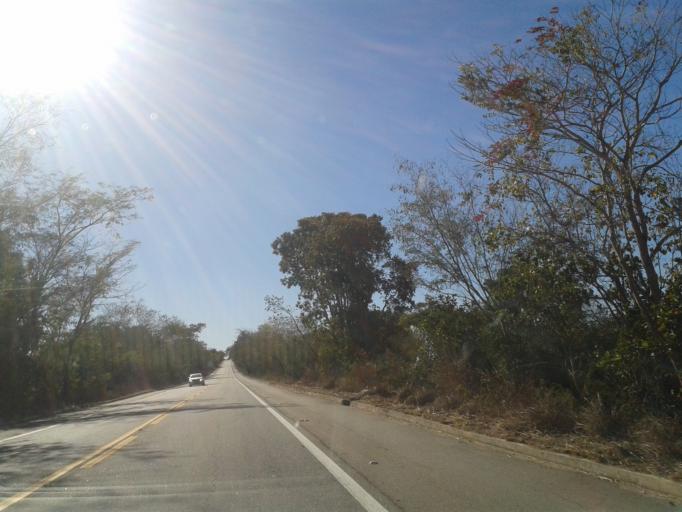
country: BR
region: Goias
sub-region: Itapuranga
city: Itapuranga
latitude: -15.3456
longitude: -50.4096
